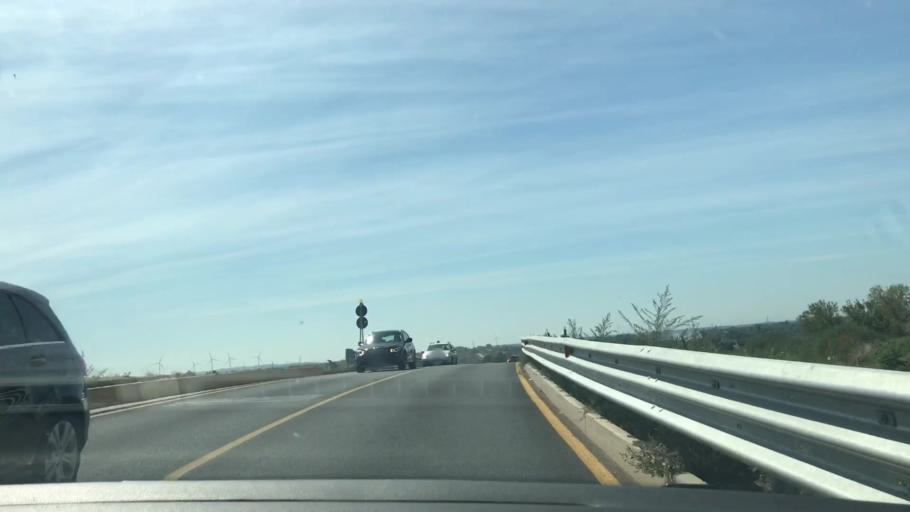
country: IT
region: Apulia
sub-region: Provincia di Bari
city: Altamura
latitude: 40.8089
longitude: 16.5557
